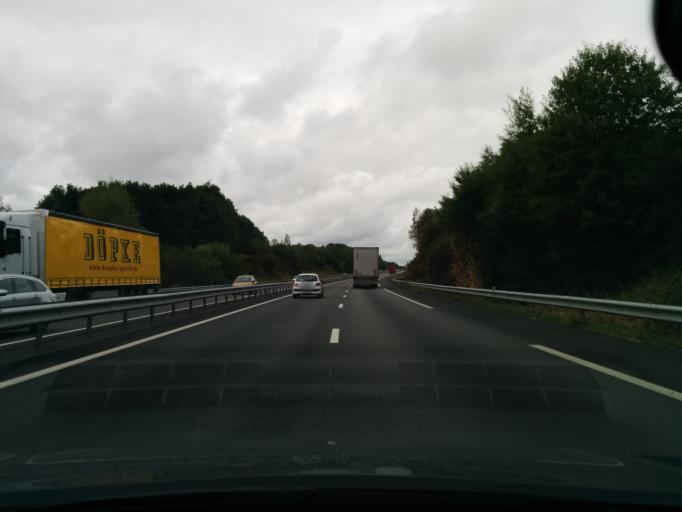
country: FR
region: Limousin
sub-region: Departement de la Haute-Vienne
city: Saint-Germain-les-Belles
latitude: 45.5633
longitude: 1.4985
